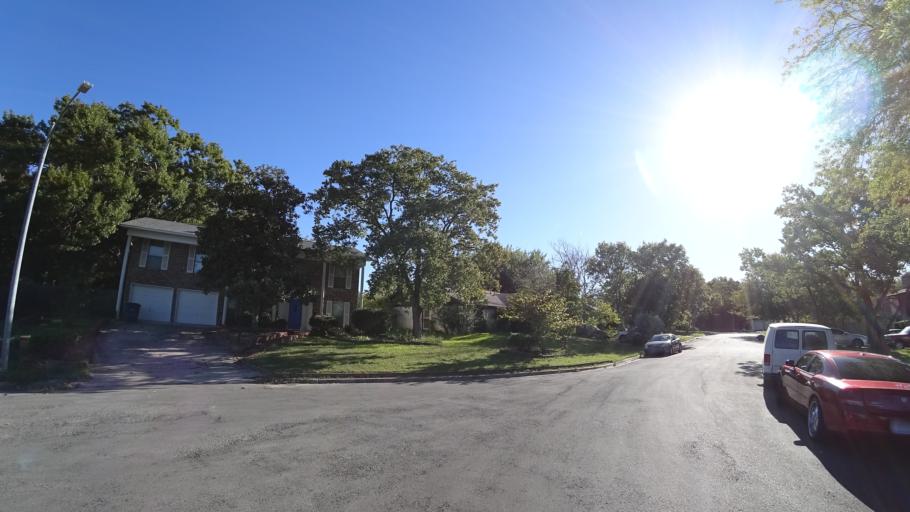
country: US
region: Texas
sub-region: Travis County
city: Austin
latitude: 30.3077
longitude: -97.6640
